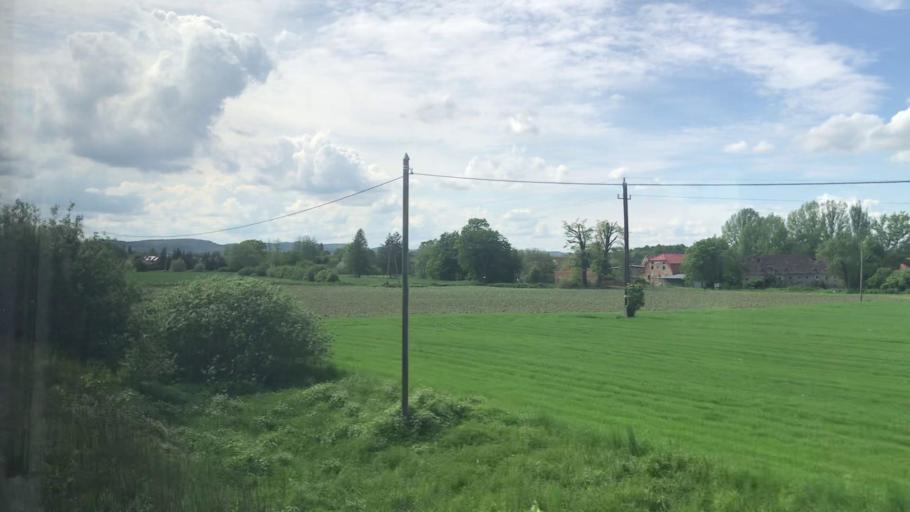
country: PL
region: Lower Silesian Voivodeship
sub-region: Powiat swidnicki
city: Swiebodzice
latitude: 50.8753
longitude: 16.3680
